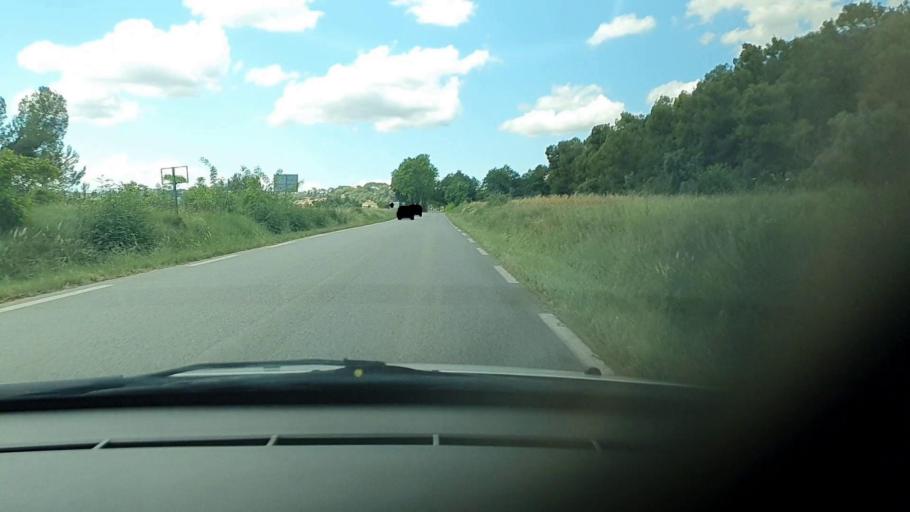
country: FR
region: Languedoc-Roussillon
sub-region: Departement du Gard
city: Montaren-et-Saint-Mediers
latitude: 44.0331
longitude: 4.3673
